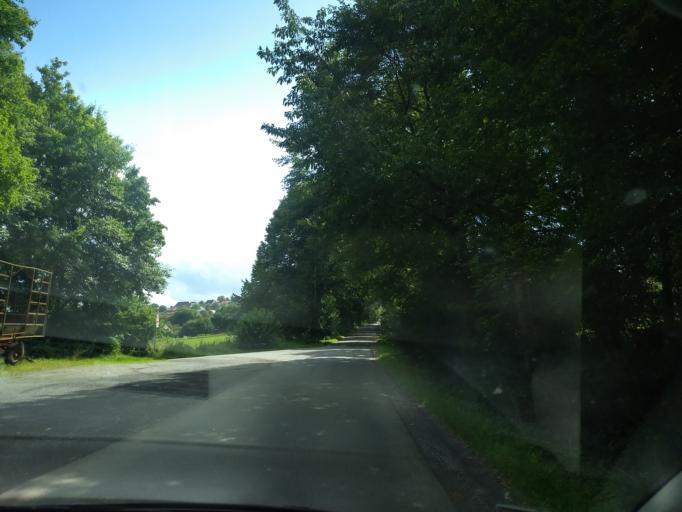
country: DE
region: North Rhine-Westphalia
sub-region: Regierungsbezirk Detmold
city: Buren
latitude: 51.5273
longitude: 8.5257
